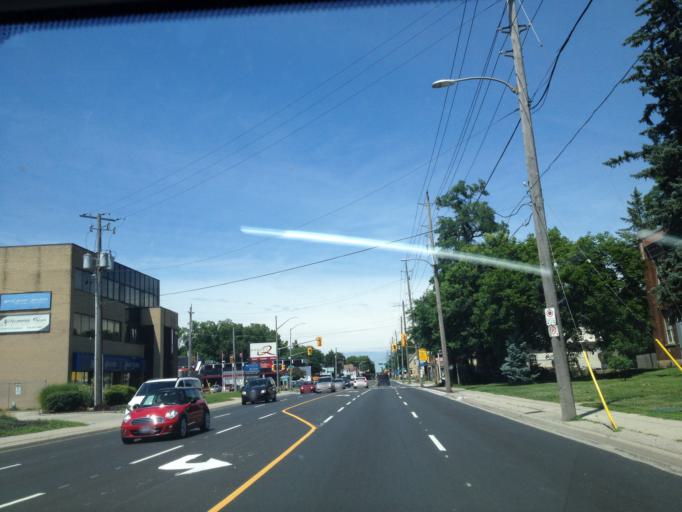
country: CA
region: Ontario
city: London
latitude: 42.9728
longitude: -81.2620
